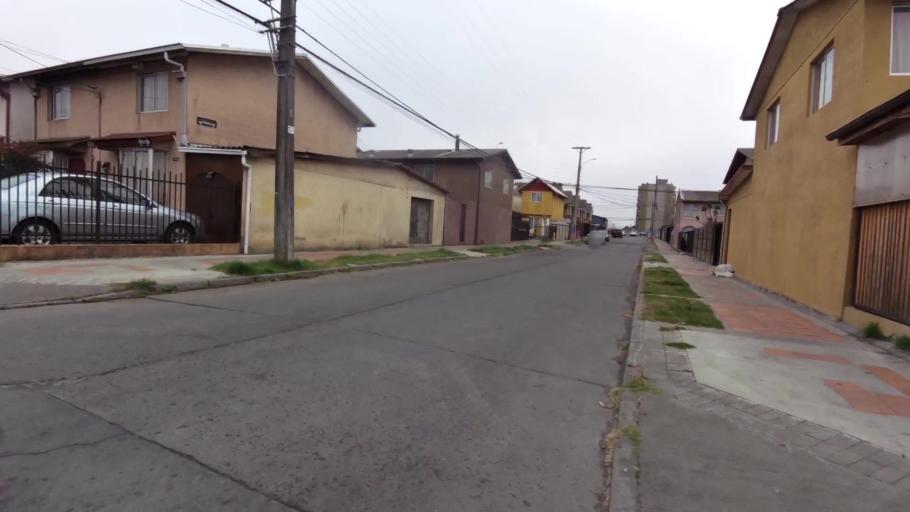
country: CL
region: Biobio
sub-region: Provincia de Concepcion
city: Concepcion
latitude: -36.7922
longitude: -73.0825
